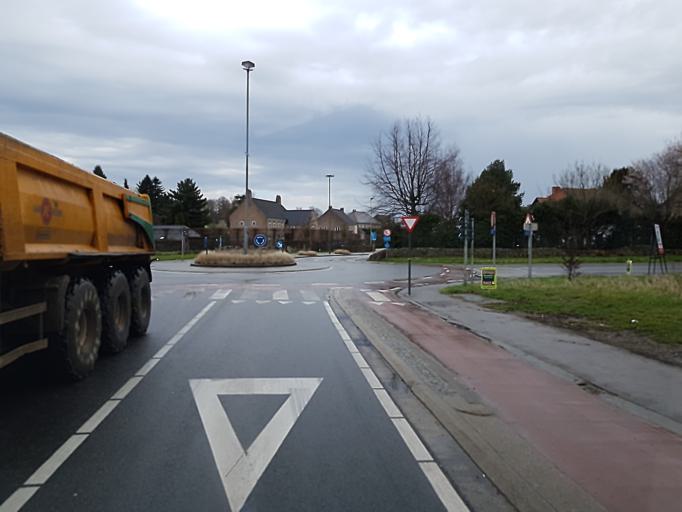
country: BE
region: Flanders
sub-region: Provincie Limburg
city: Tongeren
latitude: 50.7766
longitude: 5.4499
